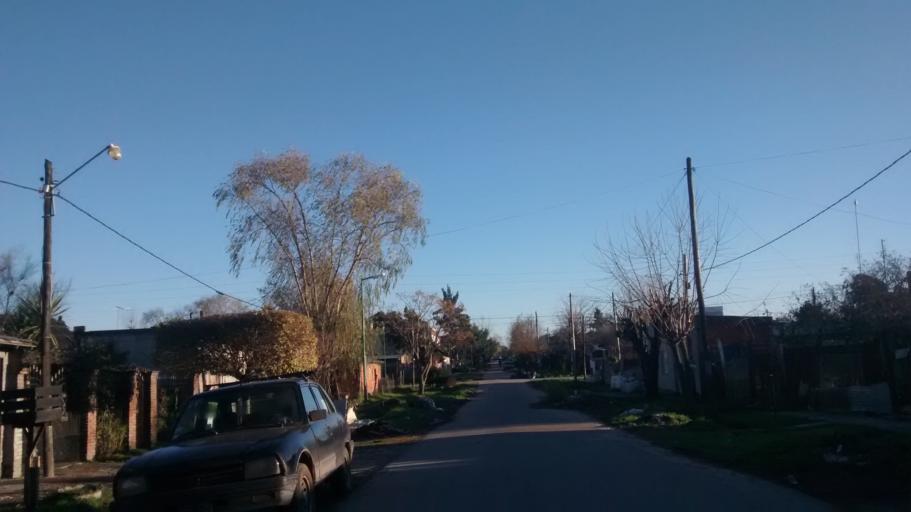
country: AR
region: Buenos Aires
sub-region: Partido de La Plata
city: La Plata
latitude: -34.9611
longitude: -57.9344
